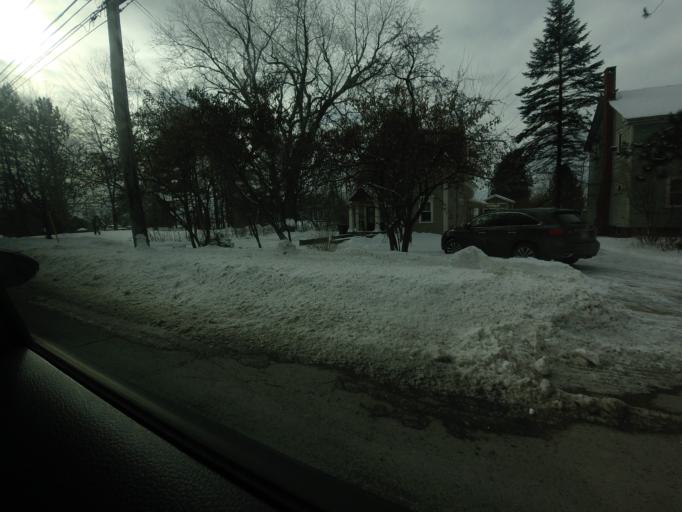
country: CA
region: New Brunswick
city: Fredericton
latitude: 45.9638
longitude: -66.6263
